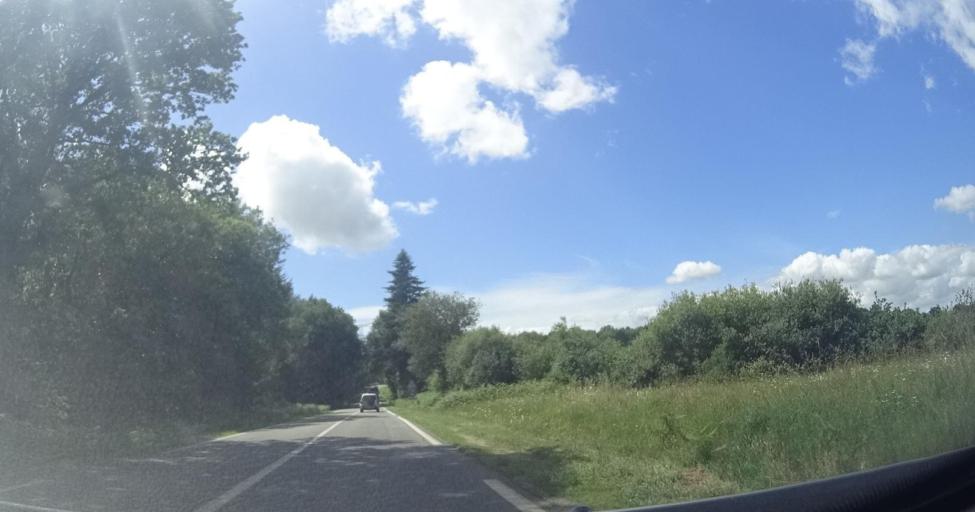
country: FR
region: Brittany
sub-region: Departement du Morbihan
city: Pluherlin
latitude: 47.6761
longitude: -2.3752
